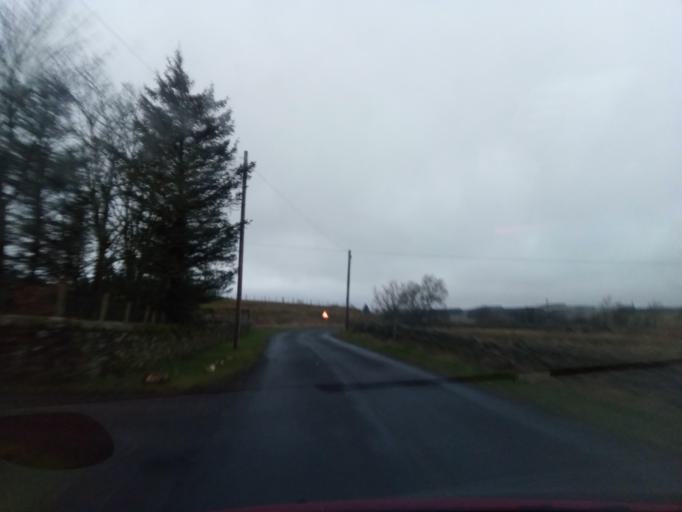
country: GB
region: England
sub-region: Northumberland
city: Otterburn
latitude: 55.2296
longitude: -2.1010
